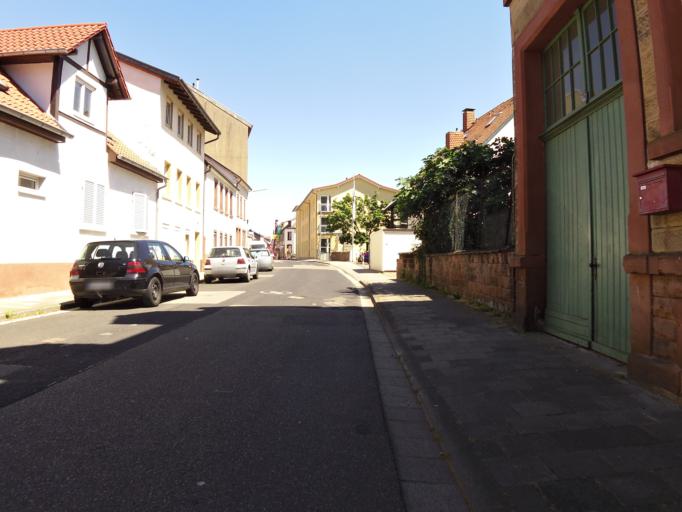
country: DE
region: Rheinland-Pfalz
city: Neustadt
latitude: 49.3532
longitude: 8.1228
